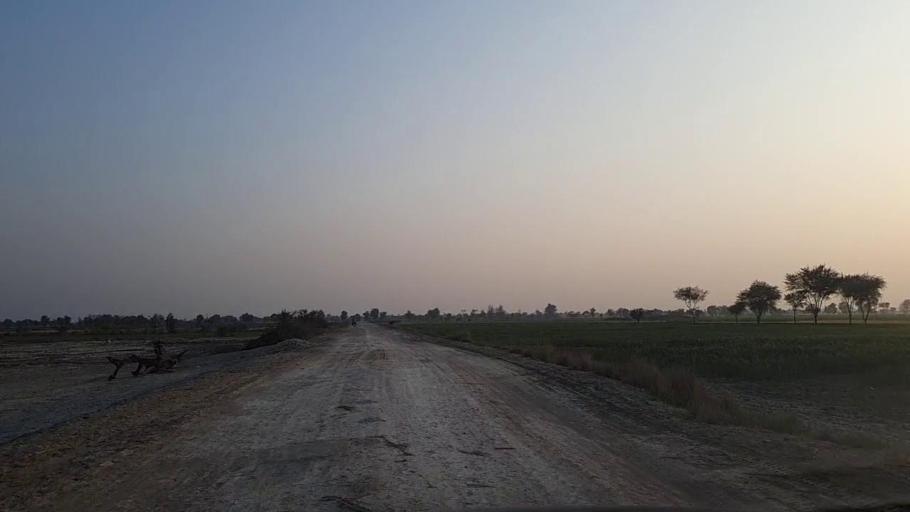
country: PK
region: Sindh
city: Daur
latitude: 26.4240
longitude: 68.3679
